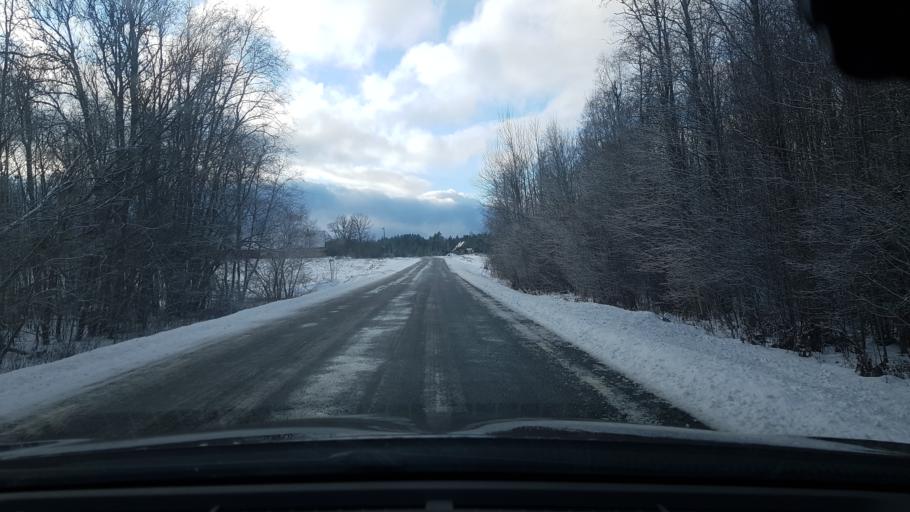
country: EE
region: Harju
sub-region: Paldiski linn
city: Paldiski
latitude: 59.2902
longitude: 24.1500
